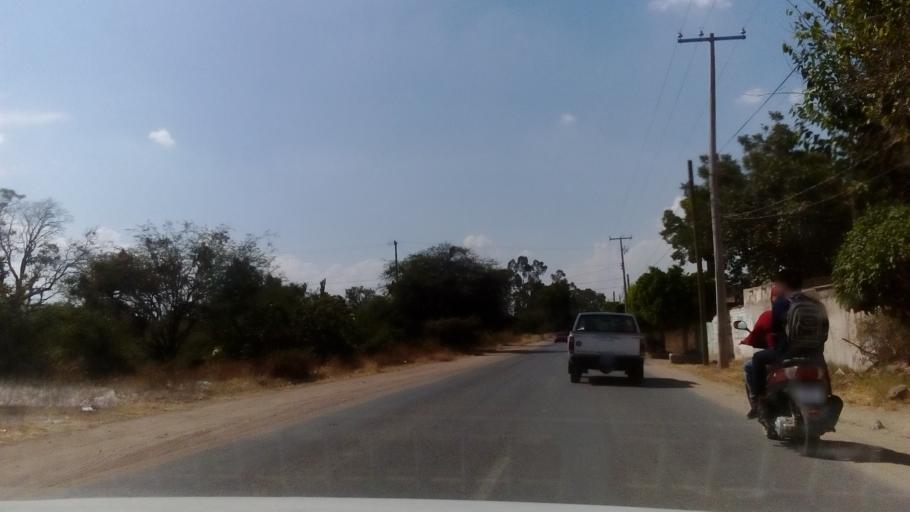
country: MX
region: Guanajuato
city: Duarte
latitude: 21.0888
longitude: -101.5306
